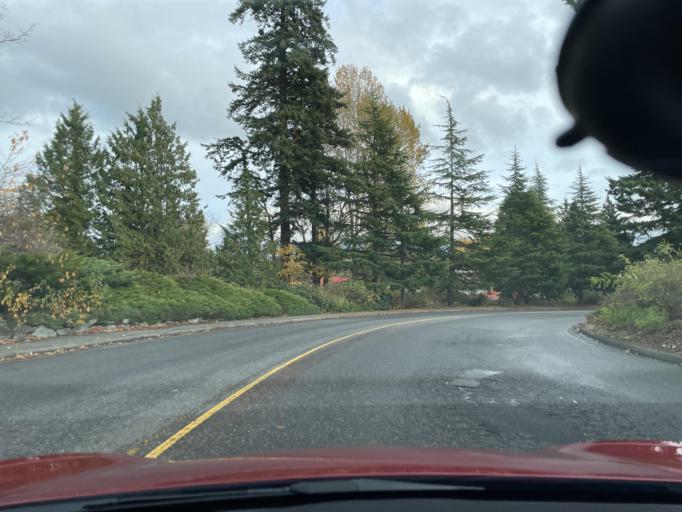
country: US
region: Washington
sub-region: Whatcom County
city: Bellingham
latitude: 48.7878
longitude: -122.4876
